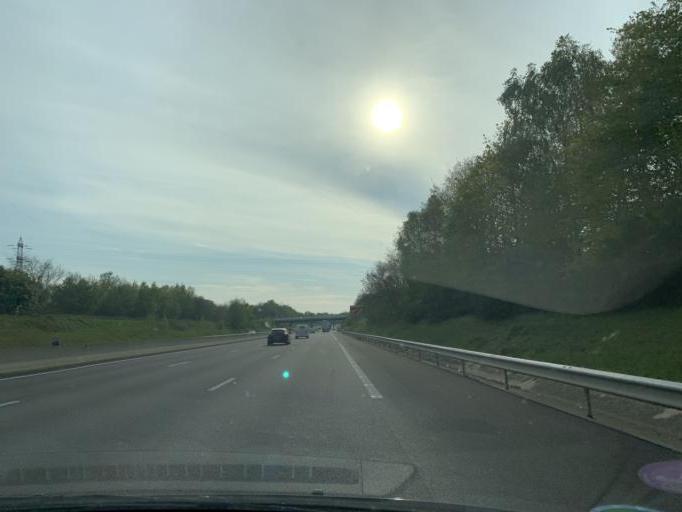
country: FR
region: Haute-Normandie
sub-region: Departement de la Seine-Maritime
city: Grand-Couronne
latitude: 49.3396
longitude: 1.0181
